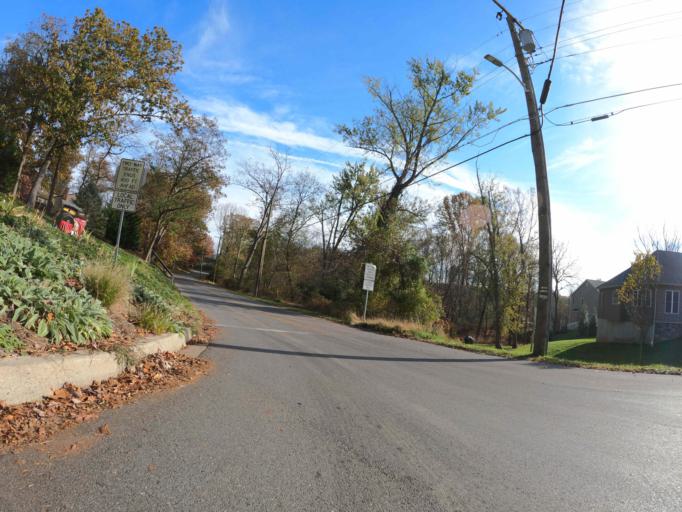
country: US
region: Maryland
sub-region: Carroll County
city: Sykesville
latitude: 39.3669
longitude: -76.9752
